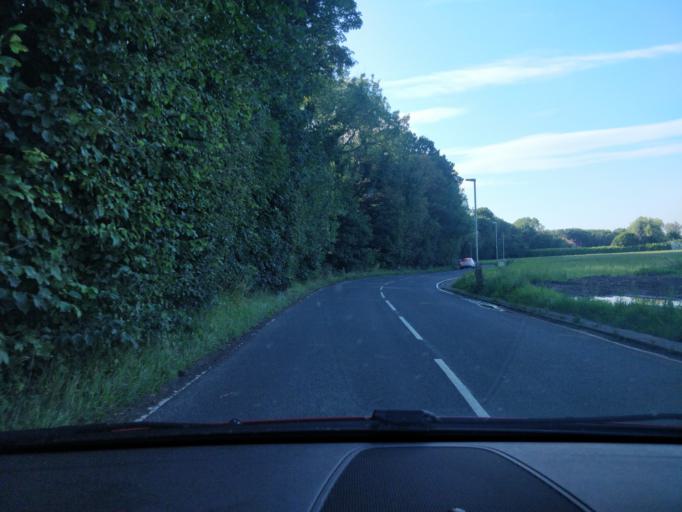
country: GB
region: England
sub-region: Lancashire
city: Banks
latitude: 53.6525
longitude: -2.8772
